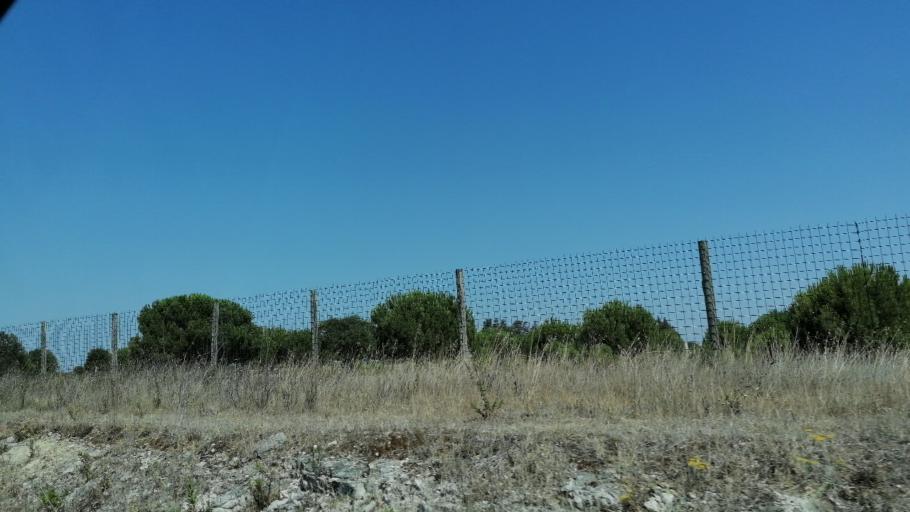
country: PT
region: Santarem
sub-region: Benavente
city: Poceirao
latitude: 38.7294
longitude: -8.7027
